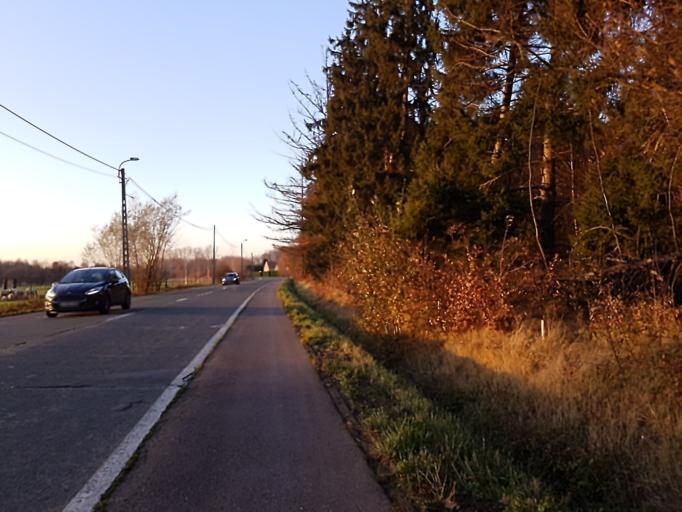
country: BE
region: Flanders
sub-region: Provincie Antwerpen
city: Bonheiden
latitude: 51.0065
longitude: 4.5432
